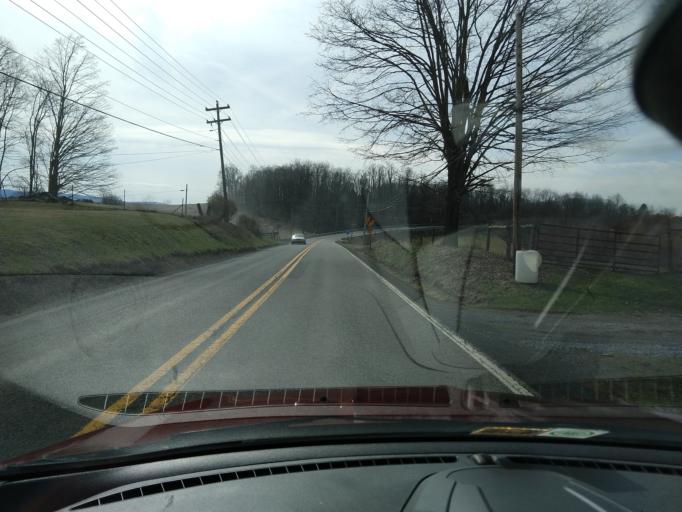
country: US
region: West Virginia
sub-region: Greenbrier County
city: Lewisburg
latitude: 37.8777
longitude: -80.4116
